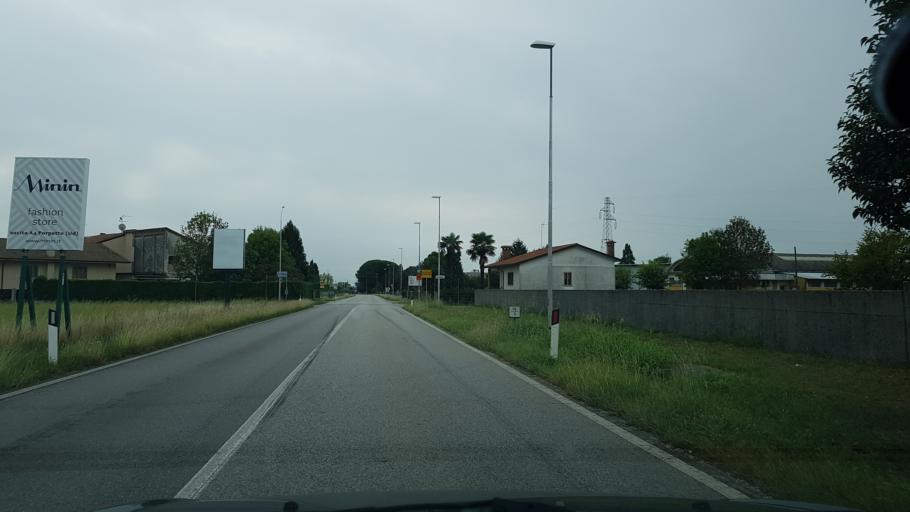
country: IT
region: Friuli Venezia Giulia
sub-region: Provincia di Udine
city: Chiopris
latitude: 45.9434
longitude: 13.3933
